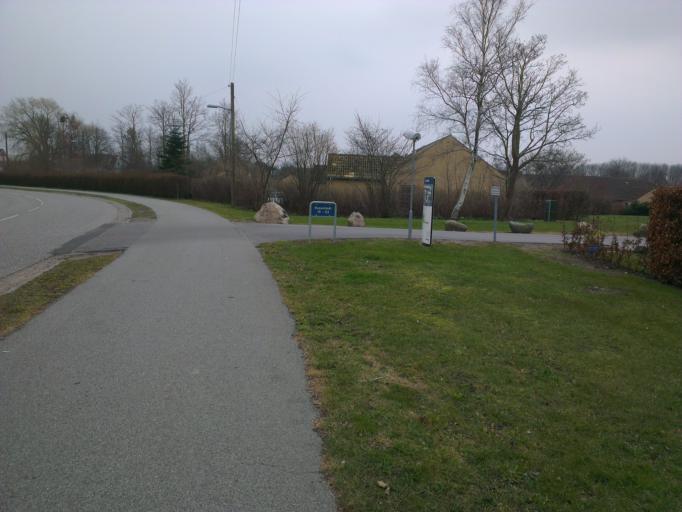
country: DK
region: Capital Region
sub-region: Frederikssund Kommune
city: Frederikssund
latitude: 55.8206
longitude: 12.0936
